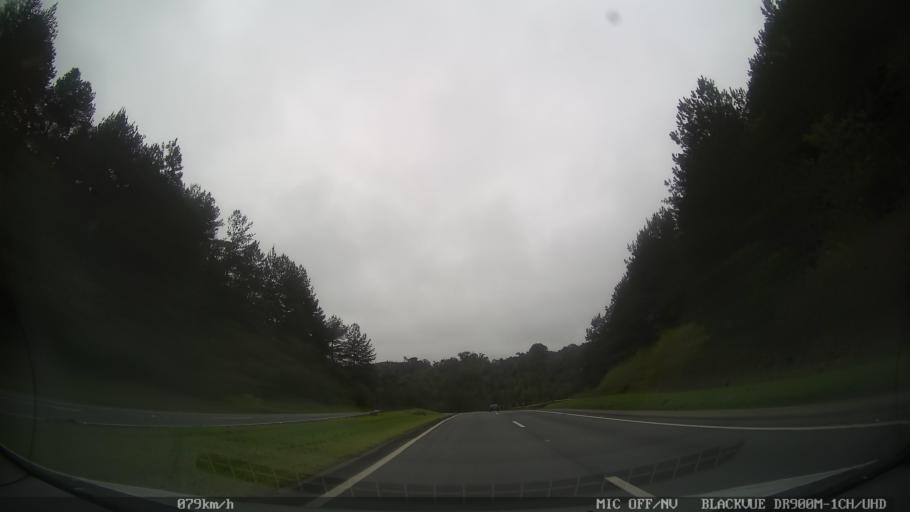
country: BR
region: Parana
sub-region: Antonina
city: Antonina
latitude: -25.0669
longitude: -48.5773
